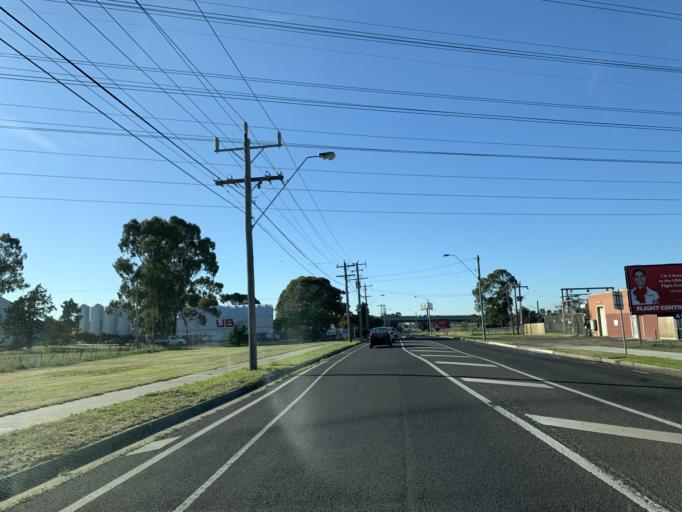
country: AU
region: Victoria
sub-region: Brimbank
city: Sunshine North
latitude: -37.7631
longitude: 144.8143
